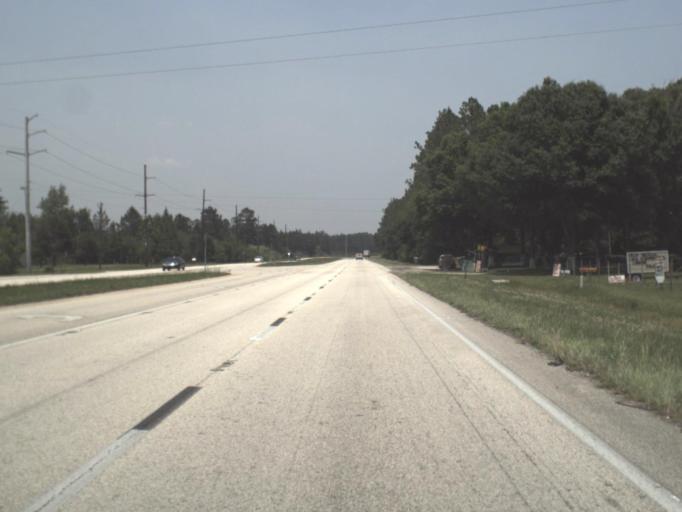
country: US
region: Florida
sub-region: Bradford County
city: Starke
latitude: 30.0803
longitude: -82.0637
